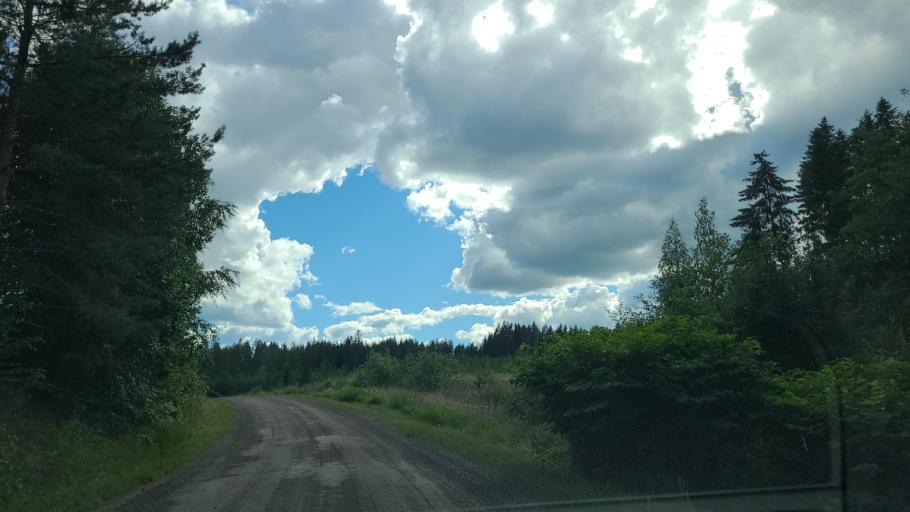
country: FI
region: Central Finland
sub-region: Jaemsae
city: Jaemsae
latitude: 61.9321
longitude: 25.3281
